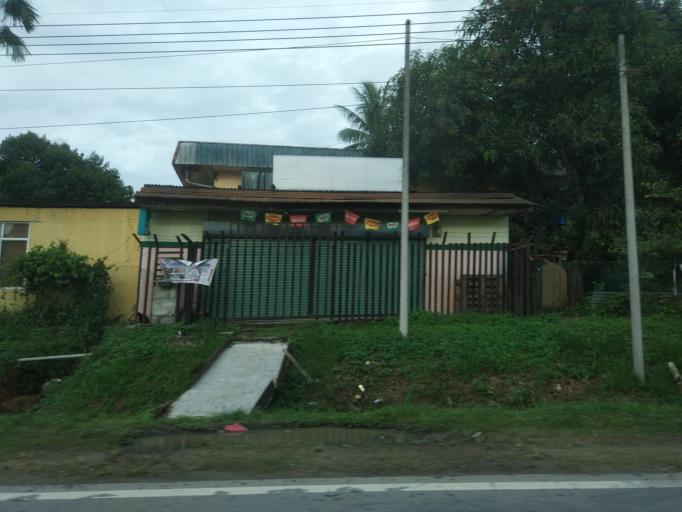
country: MY
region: Sabah
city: Kota Kinabalu
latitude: 6.1115
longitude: 116.2046
